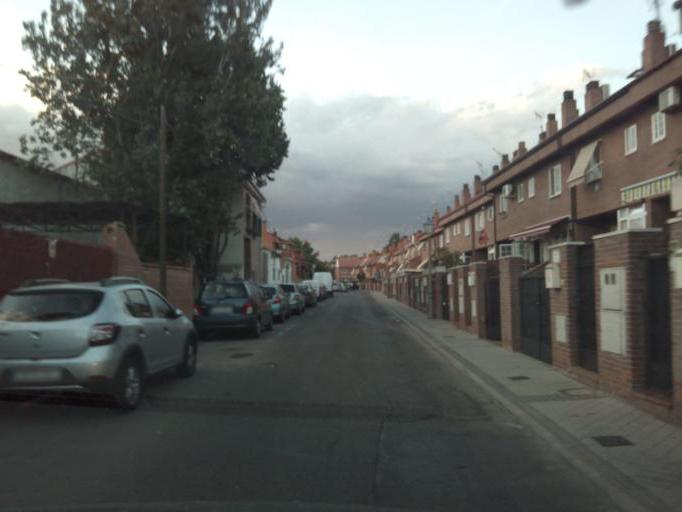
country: ES
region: Madrid
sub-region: Provincia de Madrid
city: Daganzo de Arriba
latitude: 40.5458
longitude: -3.4557
